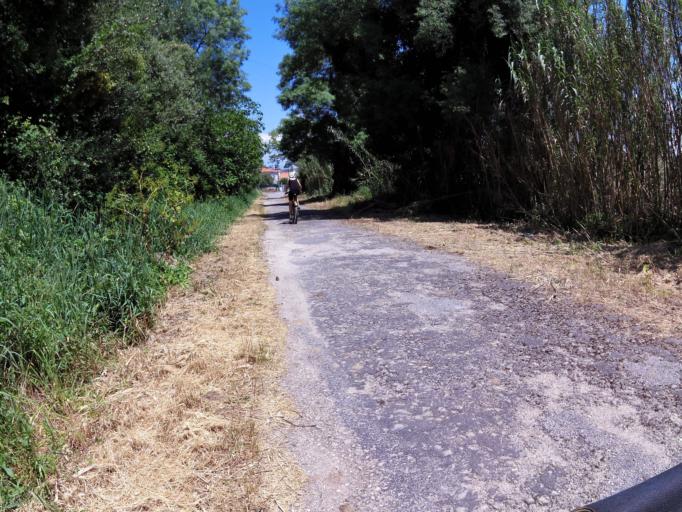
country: PT
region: Coimbra
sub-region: Montemor-O-Velho
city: Montemor-o-Velho
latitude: 40.1758
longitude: -8.6967
